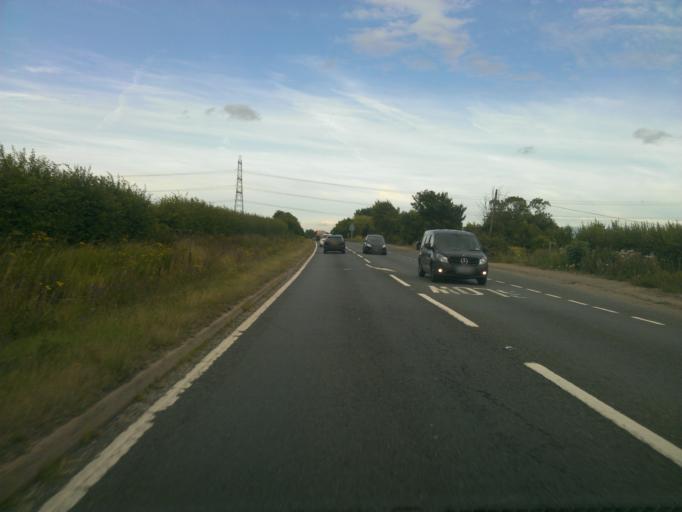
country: GB
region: England
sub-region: Essex
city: Coggeshall
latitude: 51.8746
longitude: 0.6395
